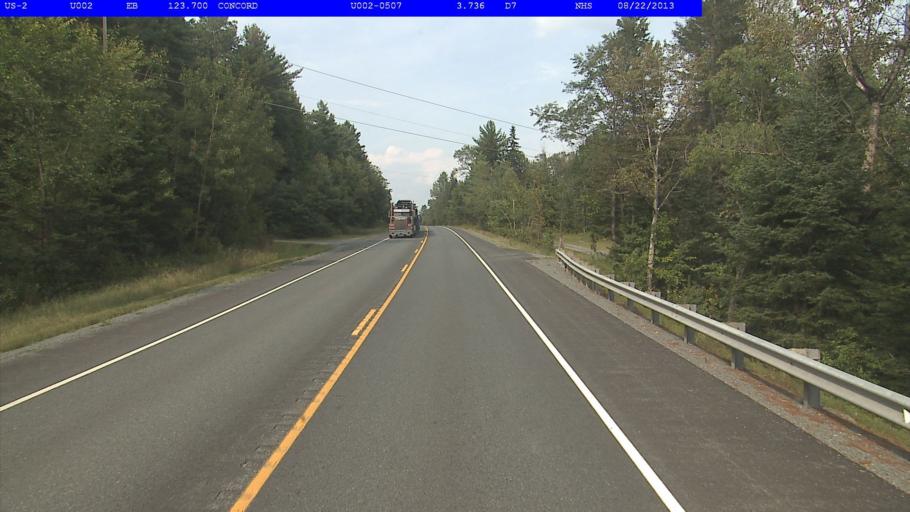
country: US
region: Vermont
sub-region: Caledonia County
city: St Johnsbury
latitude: 44.4475
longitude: -71.8745
